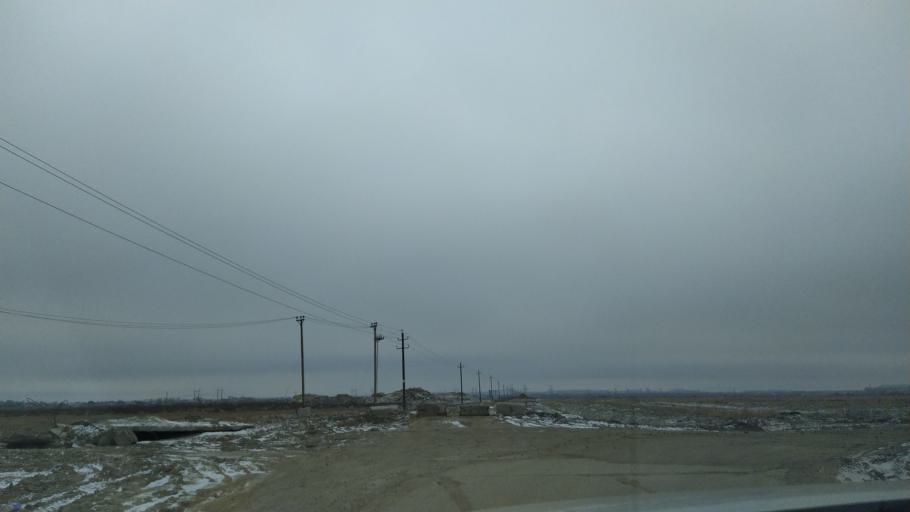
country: RU
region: St.-Petersburg
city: Aleksandrovskaya
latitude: 59.7524
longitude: 30.3603
